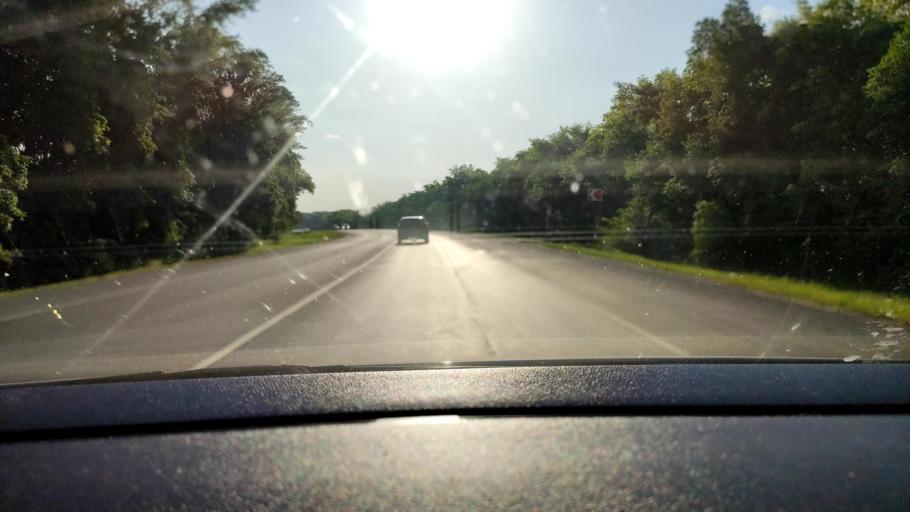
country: RU
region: Voronezj
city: Kashirskoye
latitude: 51.4905
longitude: 39.6231
